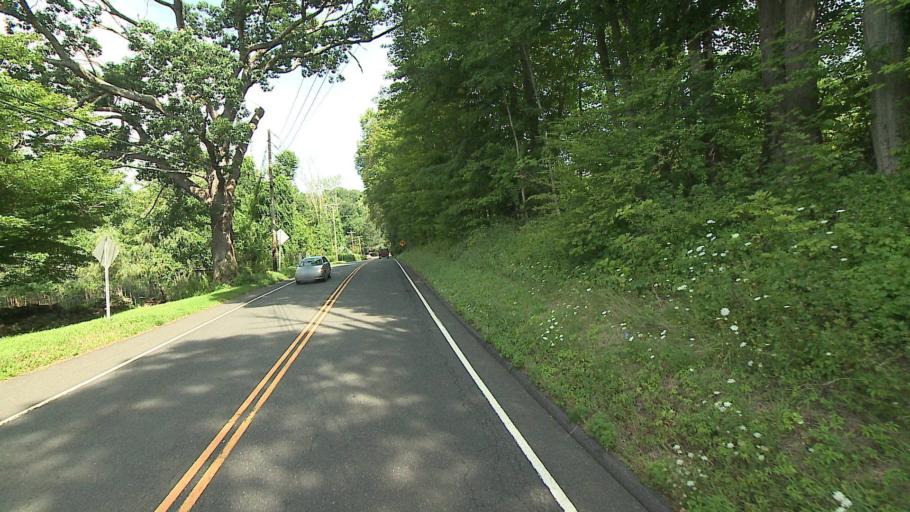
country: US
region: New York
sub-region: Putnam County
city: Putnam Lake
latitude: 41.4430
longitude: -73.5068
